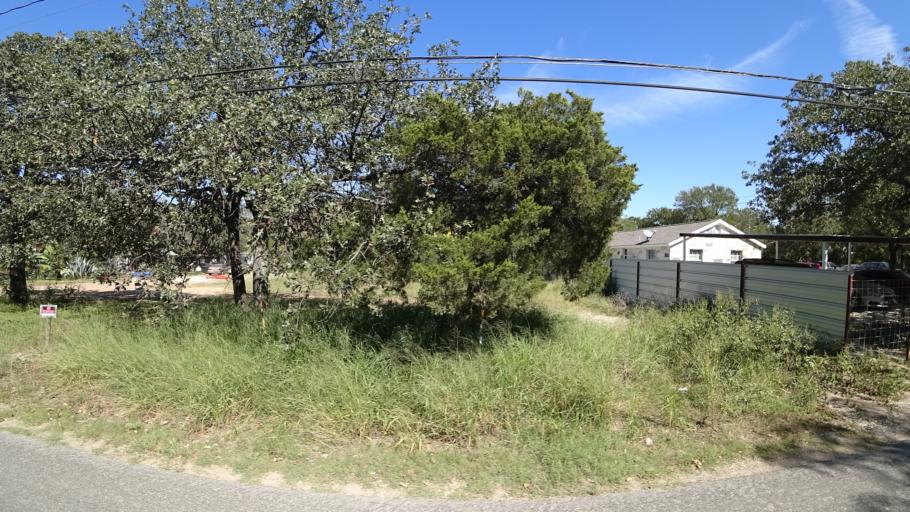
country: US
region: Texas
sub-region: Travis County
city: Austin
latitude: 30.2714
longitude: -97.6706
